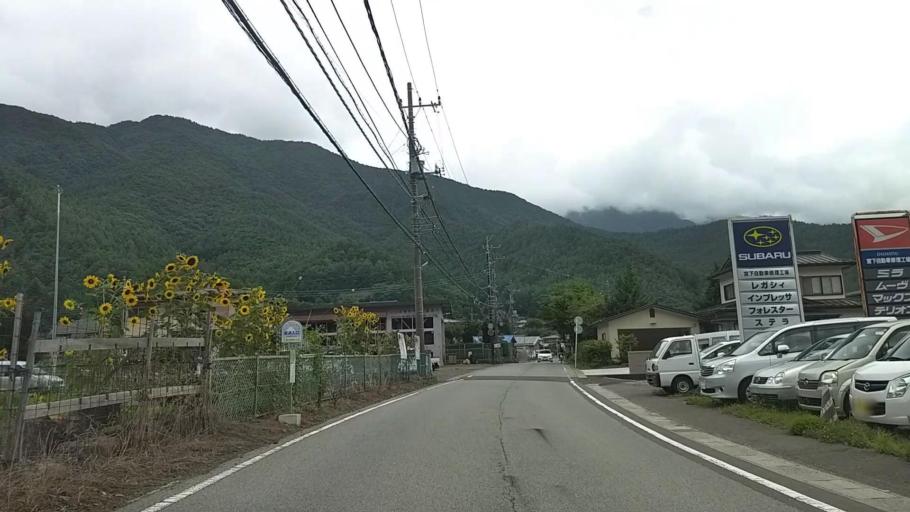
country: JP
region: Yamanashi
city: Fujikawaguchiko
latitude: 35.5054
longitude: 138.7154
